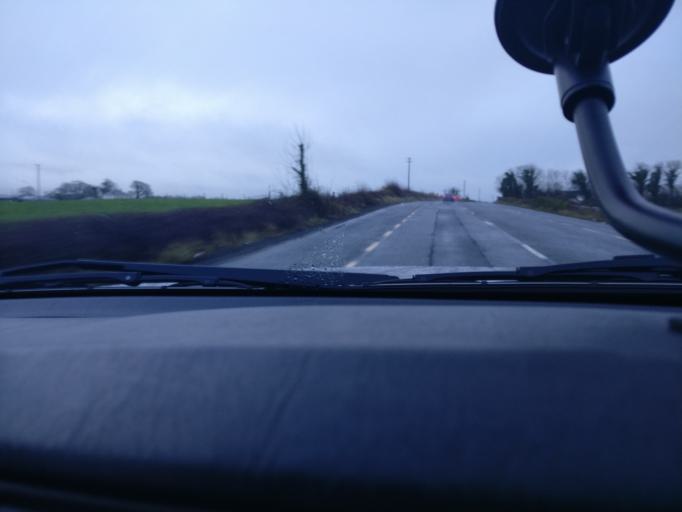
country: IE
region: Connaught
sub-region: County Galway
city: Athenry
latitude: 53.2476
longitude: -8.7667
